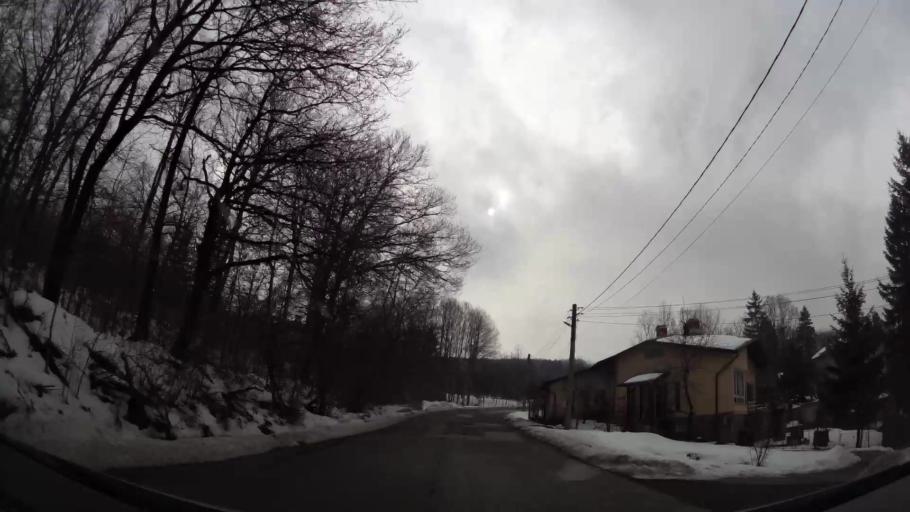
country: BG
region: Sofiya
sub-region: Obshtina Bozhurishte
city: Bozhurishte
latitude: 42.6539
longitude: 23.2005
